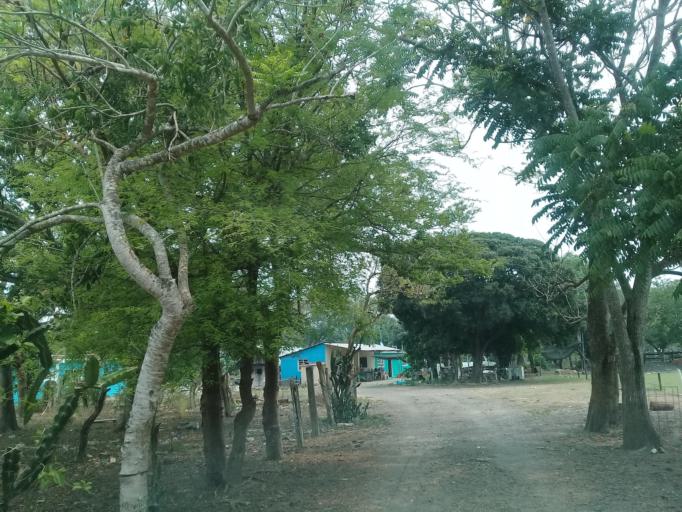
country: MX
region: Veracruz
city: Jamapa
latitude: 18.9558
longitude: -96.1958
